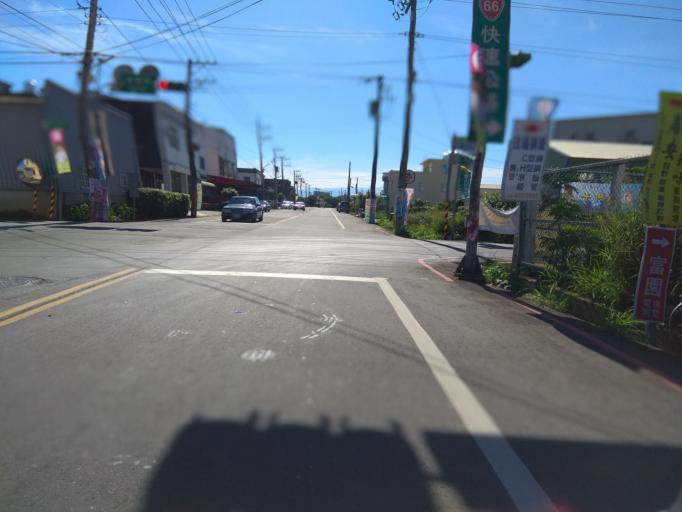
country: TW
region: Taiwan
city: Taoyuan City
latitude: 24.9820
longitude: 121.1357
